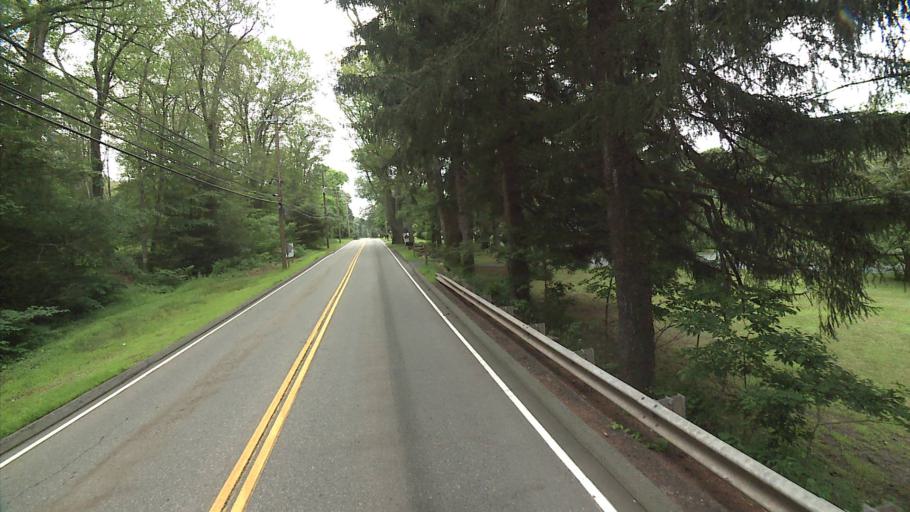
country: US
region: Connecticut
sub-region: Middlesex County
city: Higganum
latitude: 41.4876
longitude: -72.5574
